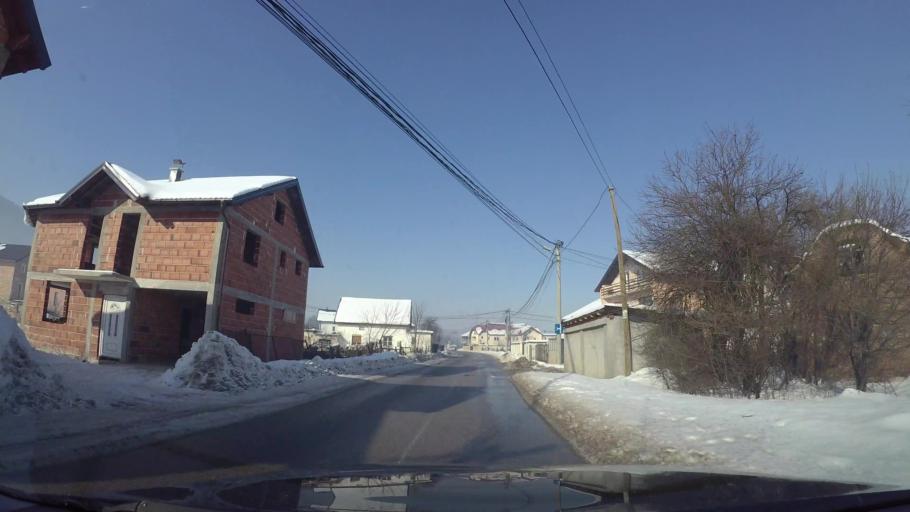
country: BA
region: Federation of Bosnia and Herzegovina
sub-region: Kanton Sarajevo
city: Sarajevo
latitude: 43.8069
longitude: 18.3008
